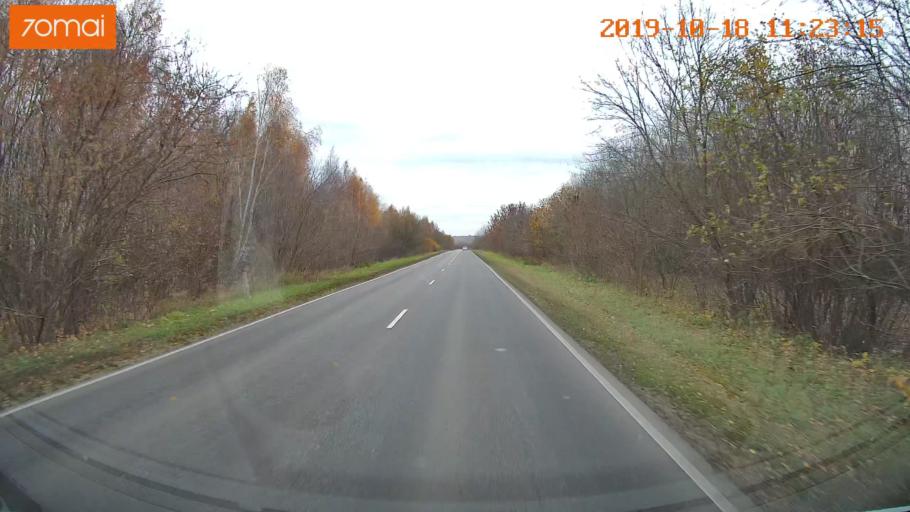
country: RU
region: Tula
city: Kimovsk
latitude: 54.0988
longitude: 38.5915
